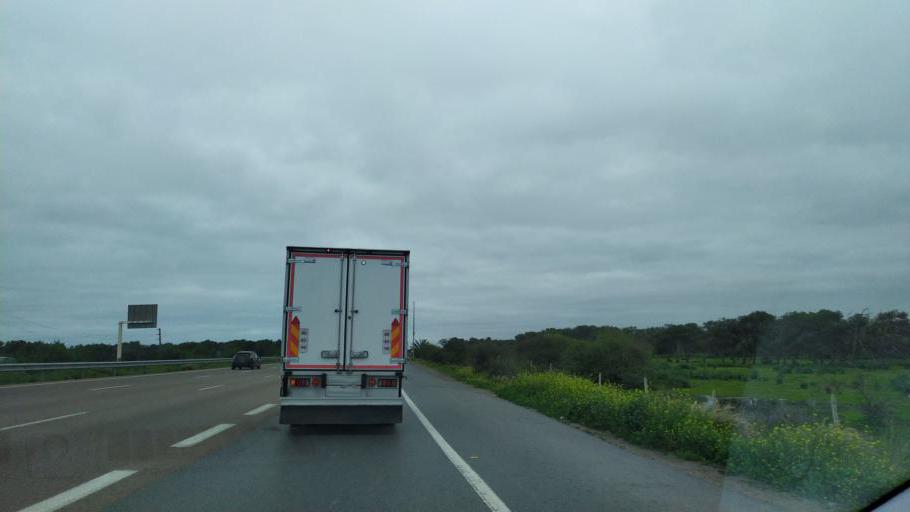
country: MA
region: Chaouia-Ouardigha
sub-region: Benslimane
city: Bouznika
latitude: 33.7798
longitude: -7.2308
